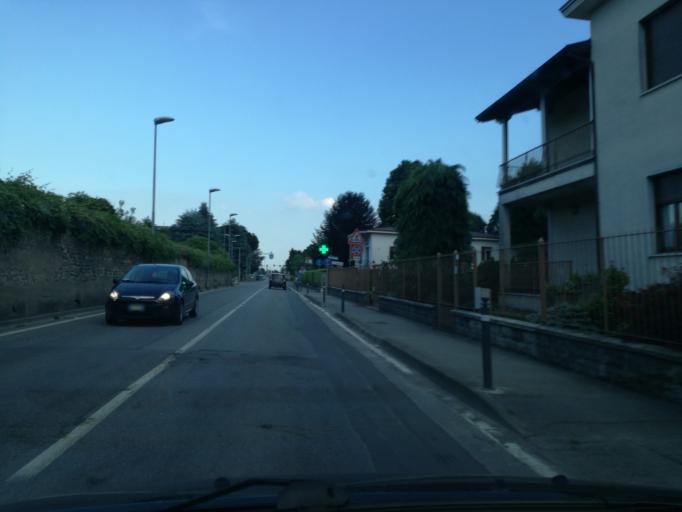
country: IT
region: Lombardy
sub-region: Provincia di Monza e Brianza
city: Cornate d'Adda
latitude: 45.6450
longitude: 9.4653
